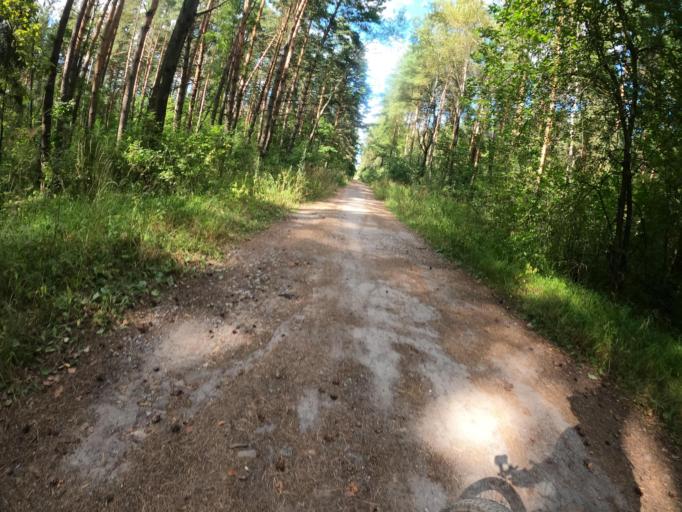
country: RU
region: Moskovskaya
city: Lopatinskiy
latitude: 55.3845
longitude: 38.7082
